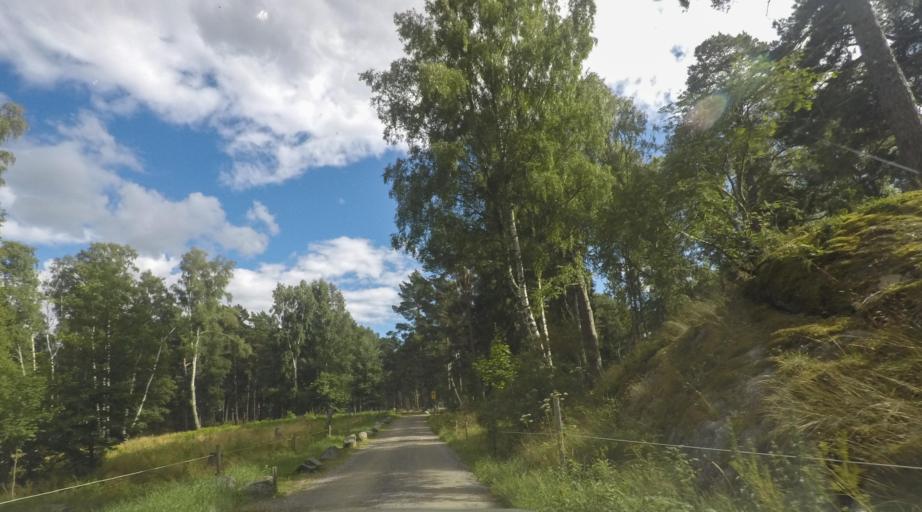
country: SE
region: Stockholm
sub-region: Sodertalje Kommun
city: Pershagen
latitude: 59.1045
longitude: 17.6792
